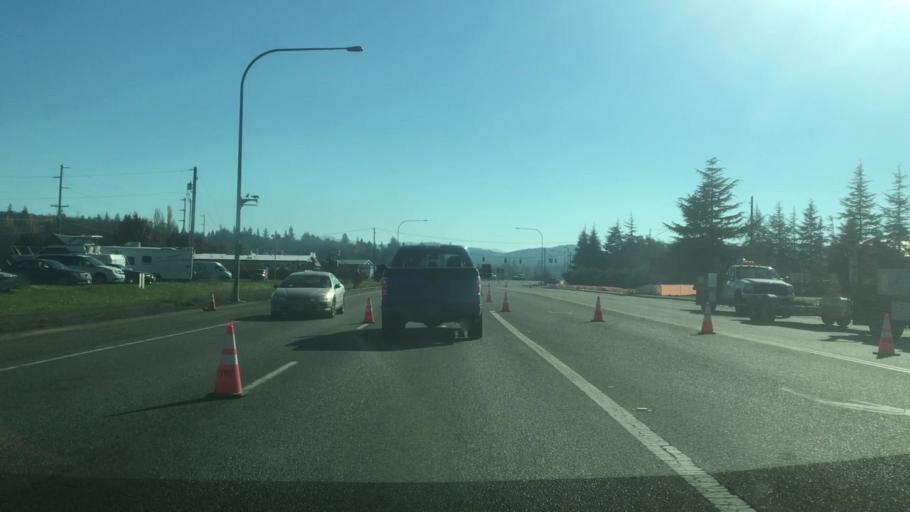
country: US
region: Washington
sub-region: Pacific County
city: Raymond
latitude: 46.6855
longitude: -123.7295
